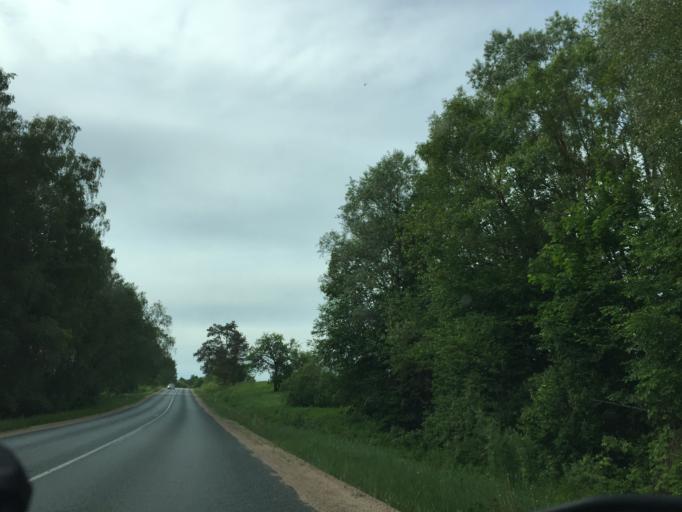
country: LV
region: Beverina
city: Murmuiza
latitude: 57.4507
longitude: 25.4277
